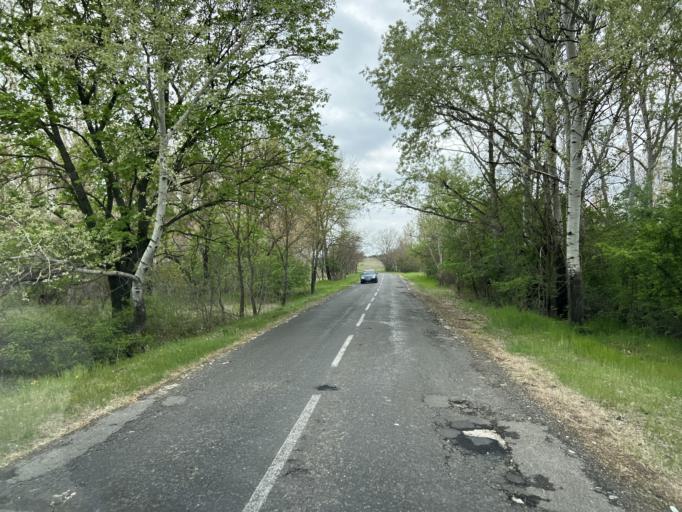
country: HU
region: Pest
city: Orkeny
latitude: 47.1030
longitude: 19.3605
